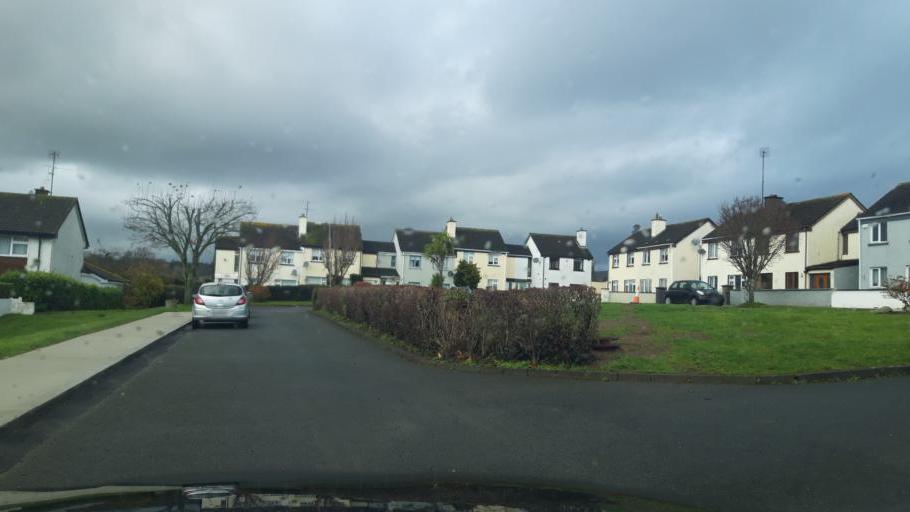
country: IE
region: Leinster
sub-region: Wicklow
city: Kilcoole
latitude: 53.1053
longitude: -6.0653
